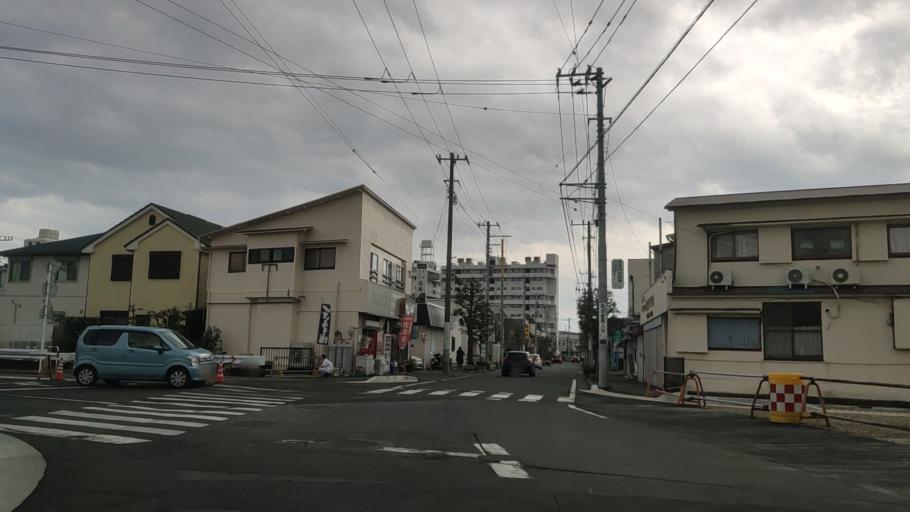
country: JP
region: Kanagawa
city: Odawara
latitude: 35.2603
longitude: 139.1605
